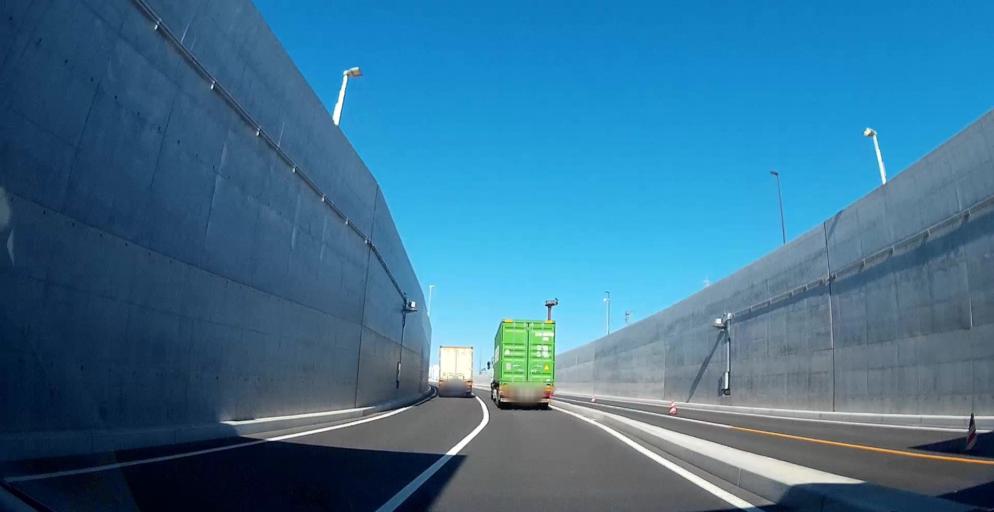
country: JP
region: Tokyo
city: Urayasu
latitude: 35.6181
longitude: 139.7950
